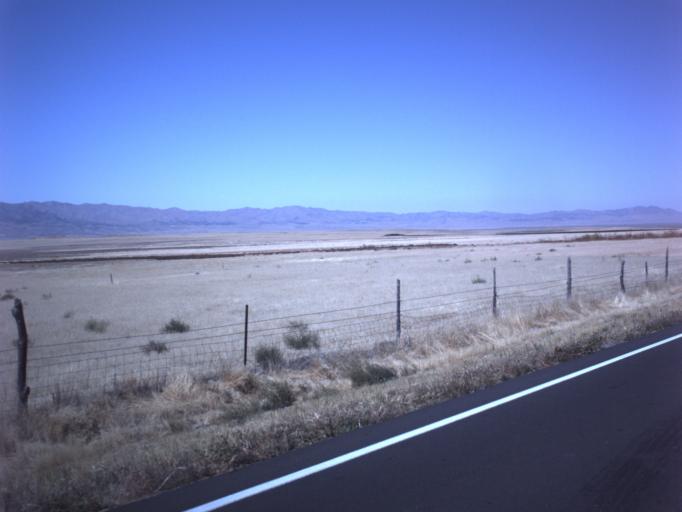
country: US
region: Utah
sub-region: Tooele County
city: Grantsville
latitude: 40.4229
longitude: -112.7488
